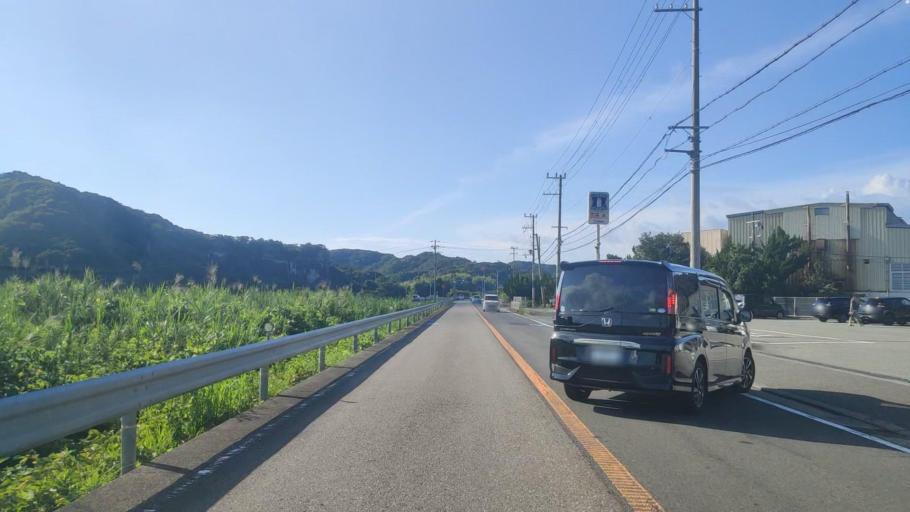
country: JP
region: Wakayama
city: Tanabe
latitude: 33.6596
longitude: 135.3999
